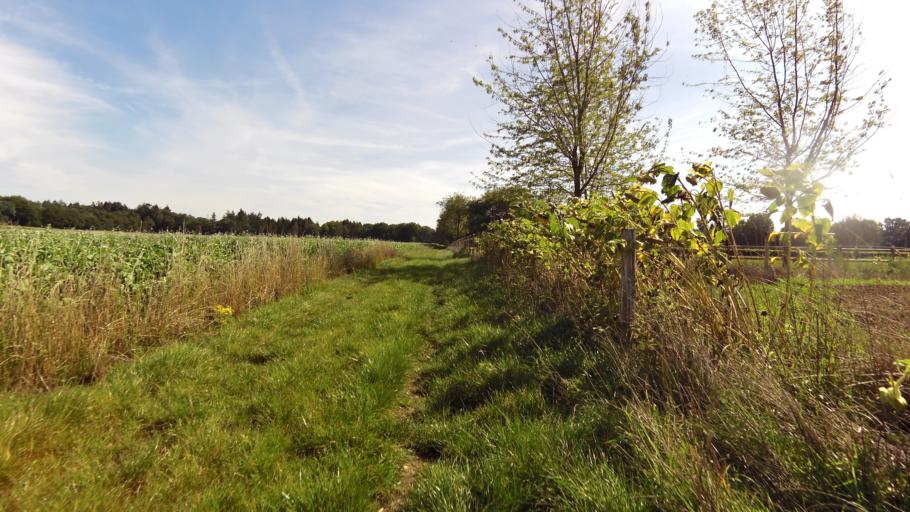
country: NL
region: Gelderland
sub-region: Gemeente Renkum
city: Renkum
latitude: 52.0142
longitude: 5.7191
